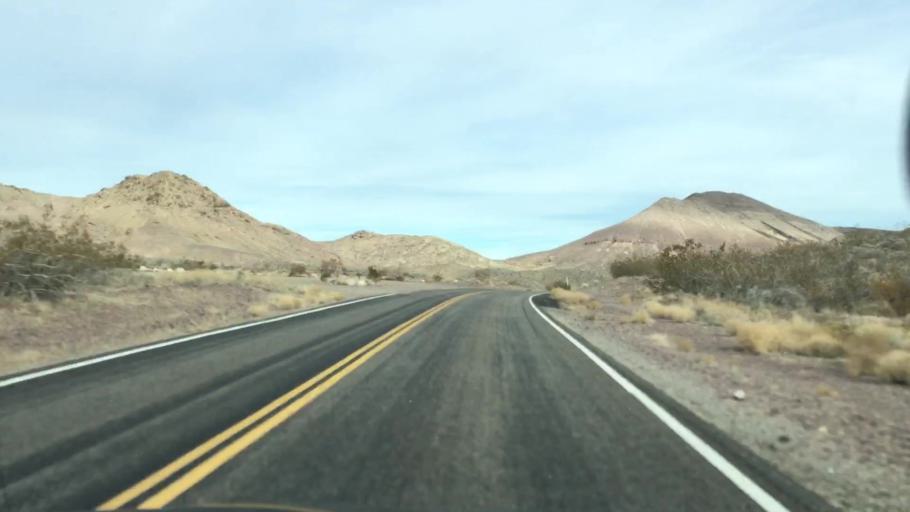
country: US
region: Nevada
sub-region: Nye County
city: Beatty
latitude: 36.7883
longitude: -116.9316
